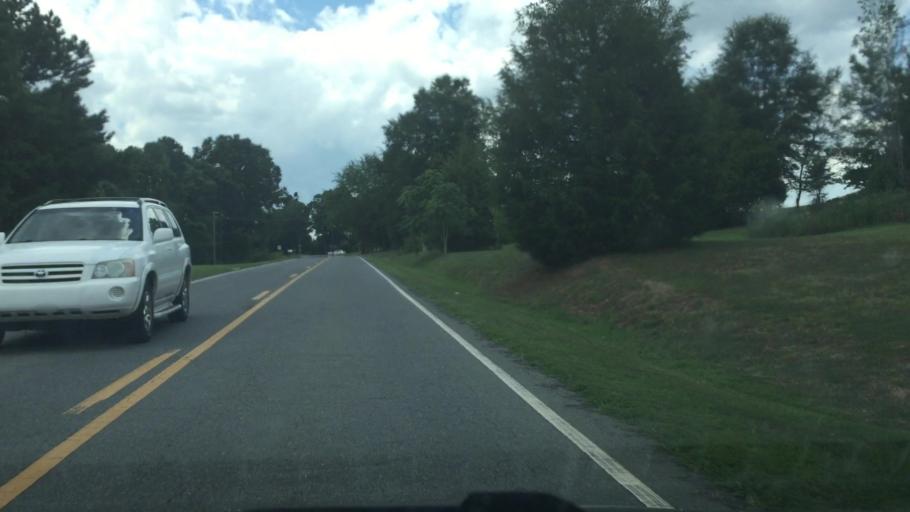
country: US
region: North Carolina
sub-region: Rowan County
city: Enochville
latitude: 35.4626
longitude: -80.7316
